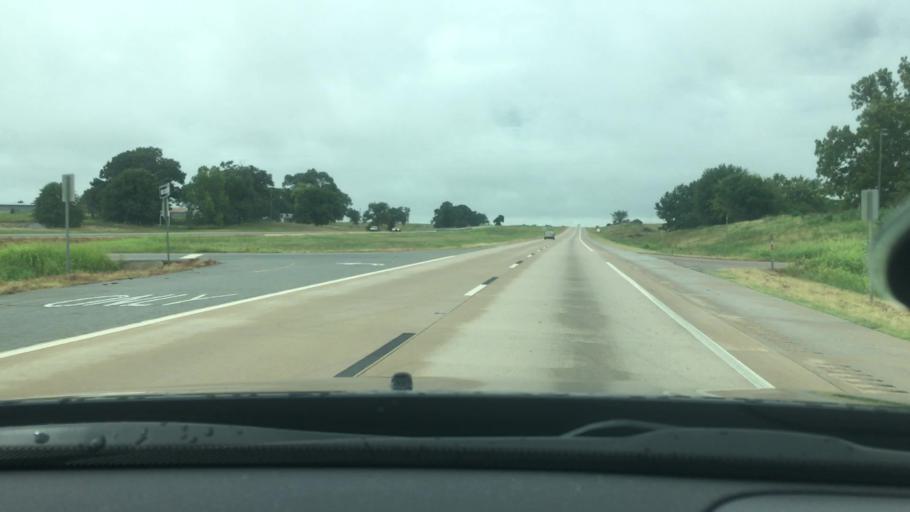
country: US
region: Oklahoma
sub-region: Atoka County
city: Atoka
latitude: 34.2303
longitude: -96.2242
